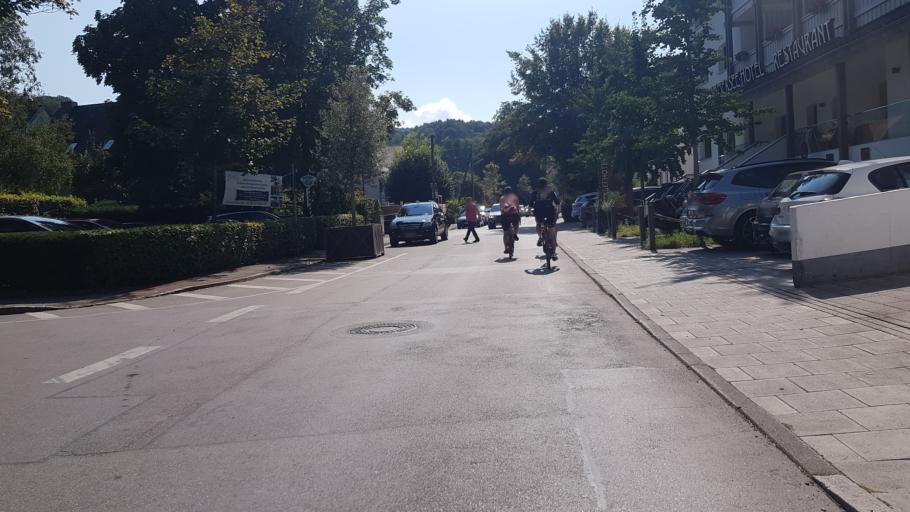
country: DE
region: Bavaria
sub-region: Upper Bavaria
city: Herrsching am Ammersee
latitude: 47.9921
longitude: 11.1711
